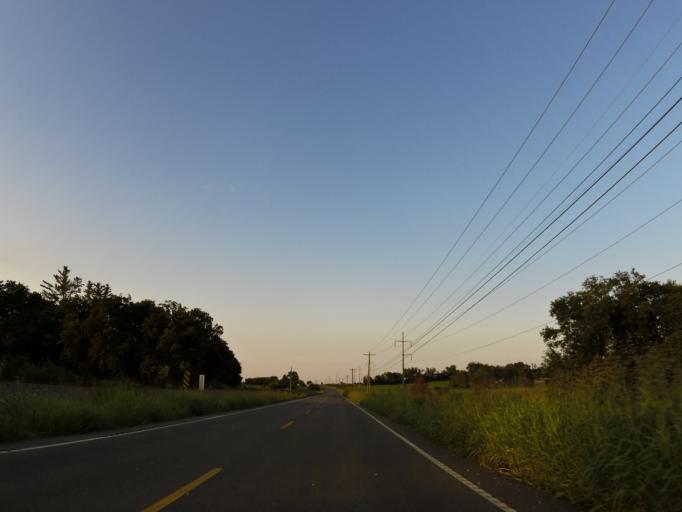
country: US
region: Tennessee
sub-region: Monroe County
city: Sweetwater
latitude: 35.6493
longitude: -84.4249
